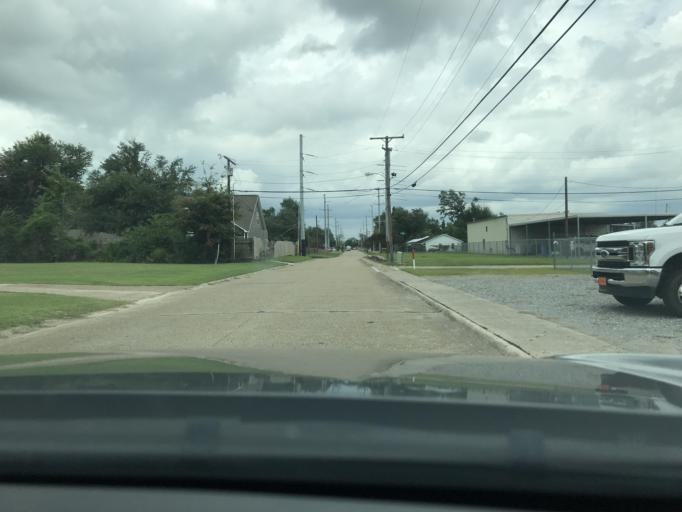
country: US
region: Louisiana
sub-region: Calcasieu Parish
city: Westlake
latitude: 30.2451
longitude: -93.2538
